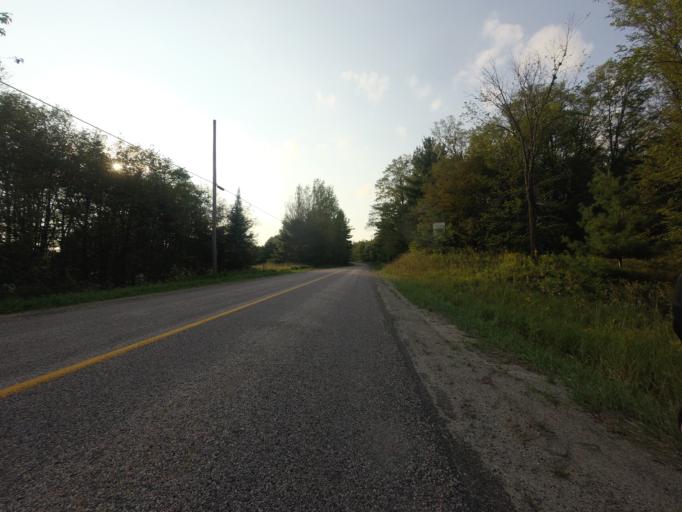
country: CA
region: Ontario
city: Renfrew
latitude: 44.9919
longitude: -76.7417
